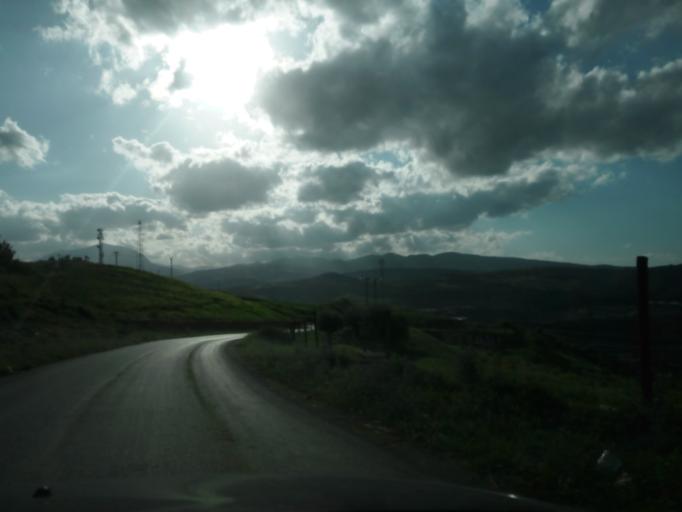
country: DZ
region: Tipaza
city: Hadjout
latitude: 36.3726
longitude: 2.4854
